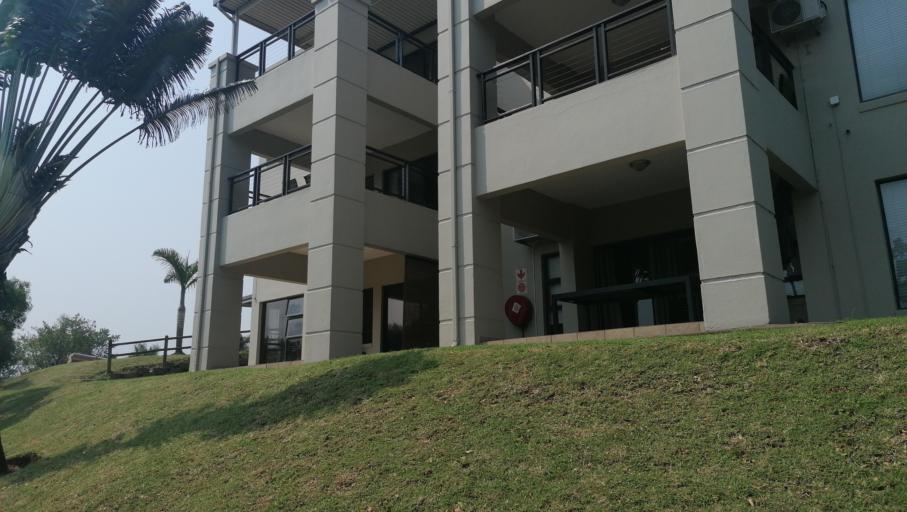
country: ZA
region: KwaZulu-Natal
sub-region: iLembe District Municipality
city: Stanger
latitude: -29.4250
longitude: 31.2503
